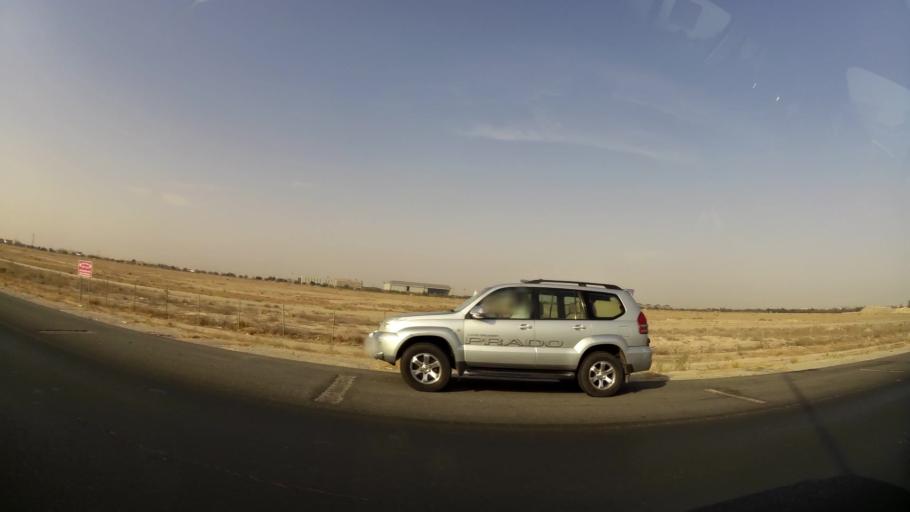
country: KW
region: Al Farwaniyah
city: Janub as Surrah
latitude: 29.2443
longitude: 47.9907
